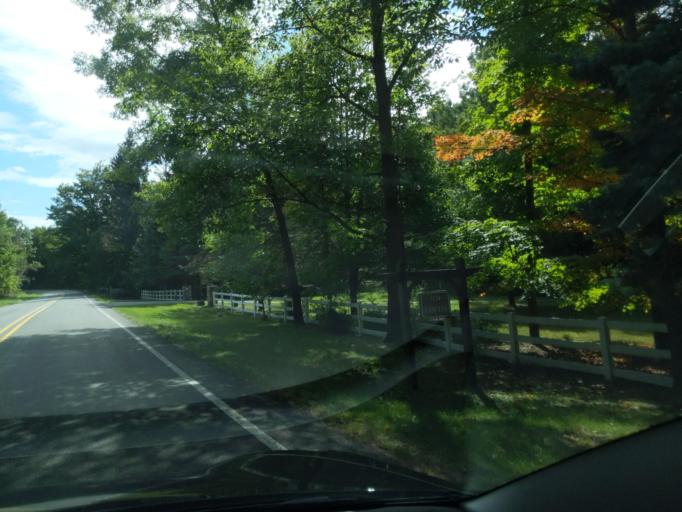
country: US
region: Michigan
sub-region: Antrim County
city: Bellaire
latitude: 44.9885
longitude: -85.2845
